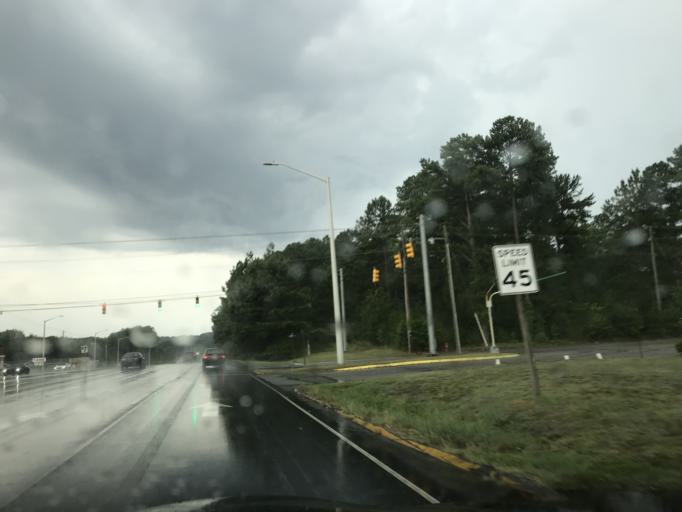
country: US
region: North Carolina
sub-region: Johnston County
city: Clayton
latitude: 35.6437
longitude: -78.4552
